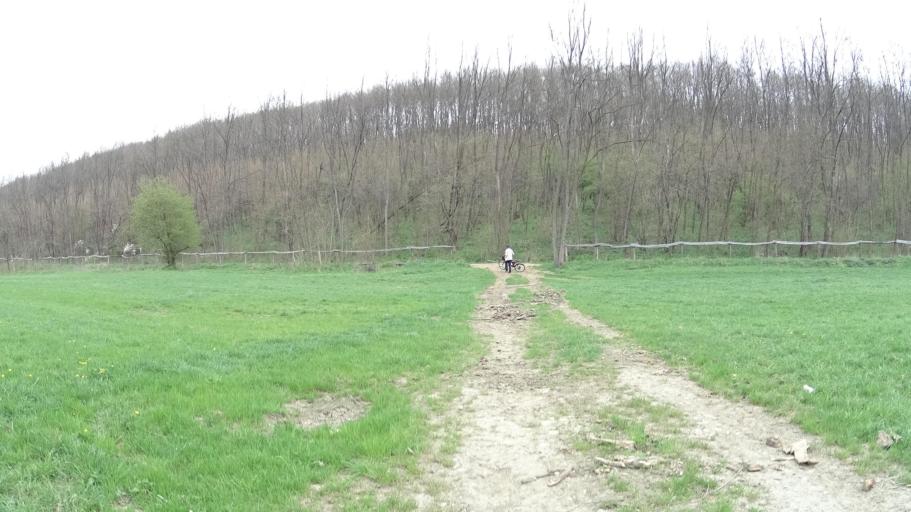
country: HU
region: Nograd
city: Diosjeno
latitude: 47.8822
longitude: 19.0621
